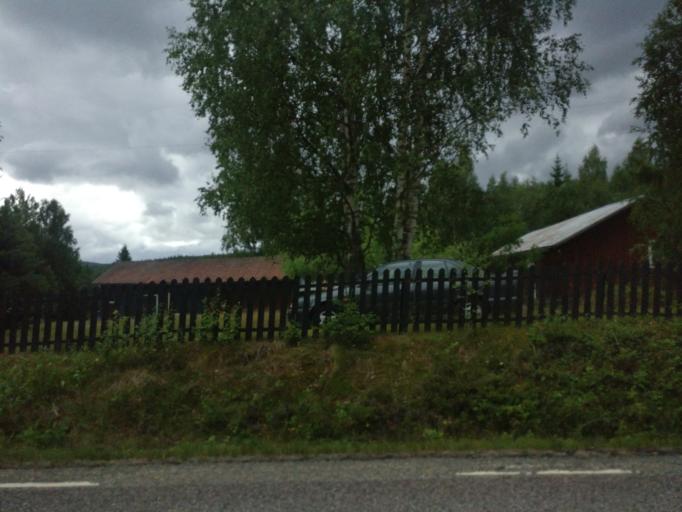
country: SE
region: Vaermland
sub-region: Torsby Kommun
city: Torsby
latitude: 60.7706
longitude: 12.7553
